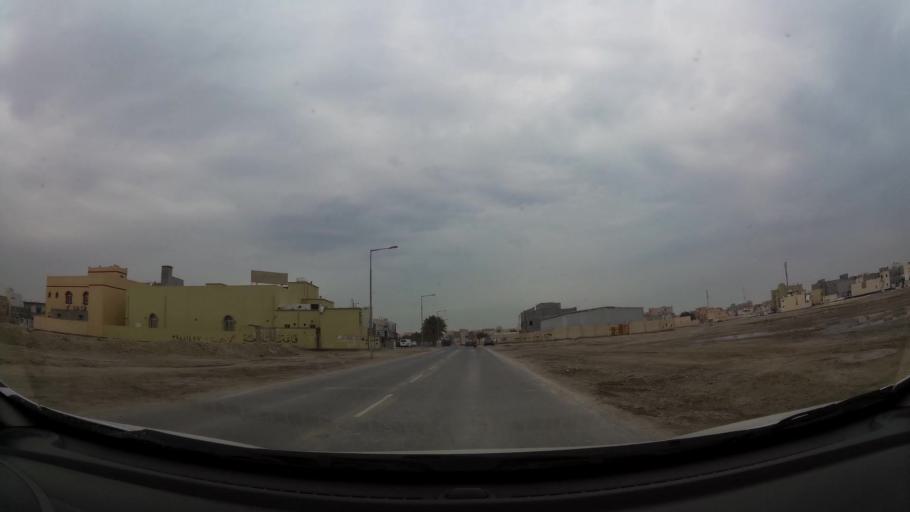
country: BH
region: Northern
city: Sitrah
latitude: 26.1652
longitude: 50.6234
